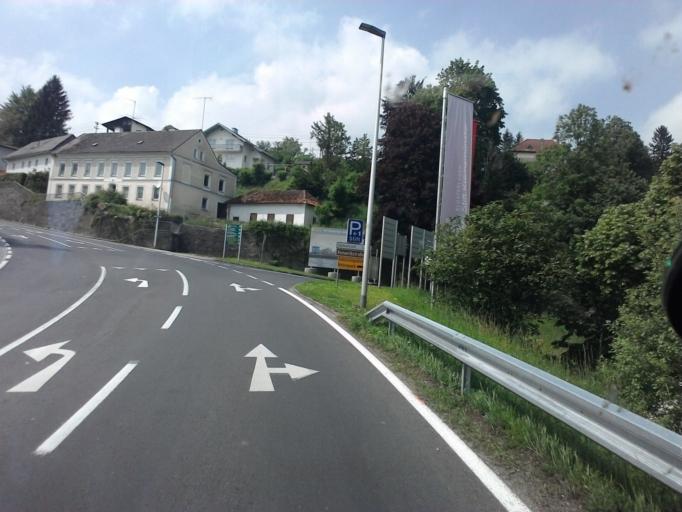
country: AT
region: Upper Austria
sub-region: Politischer Bezirk Kirchdorf an der Krems
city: Kremsmunster
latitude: 48.0545
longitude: 14.1272
